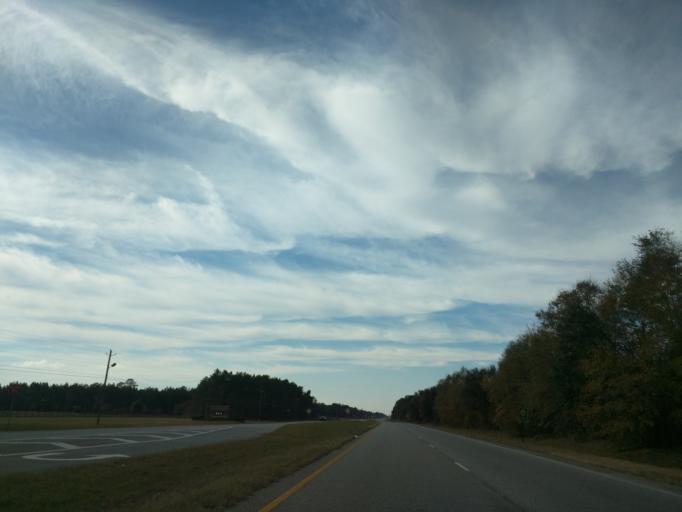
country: US
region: Georgia
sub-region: Decatur County
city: Bainbridge
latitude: 30.8879
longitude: -84.4788
